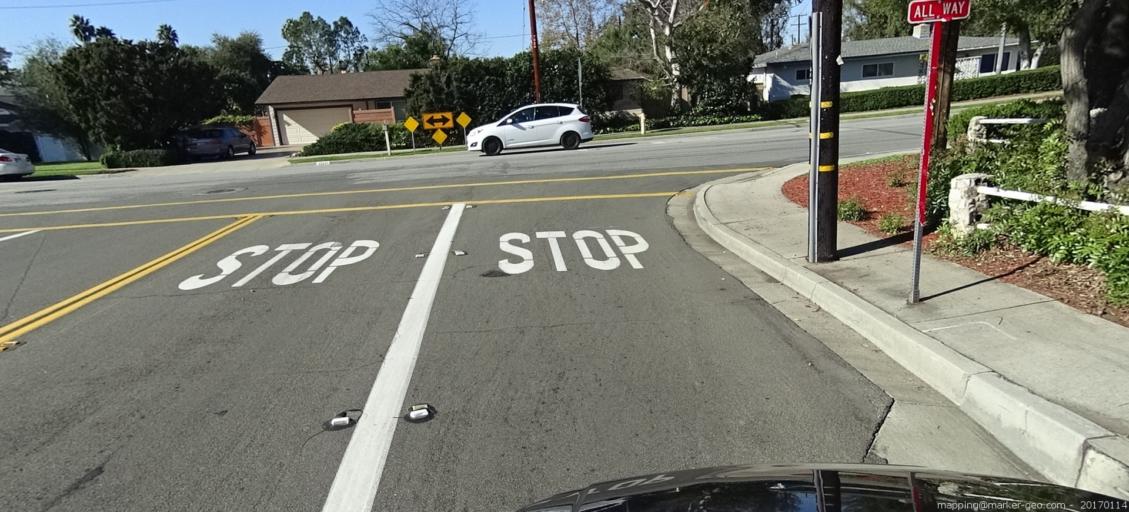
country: US
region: California
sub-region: Orange County
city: North Tustin
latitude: 33.7660
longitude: -117.8056
